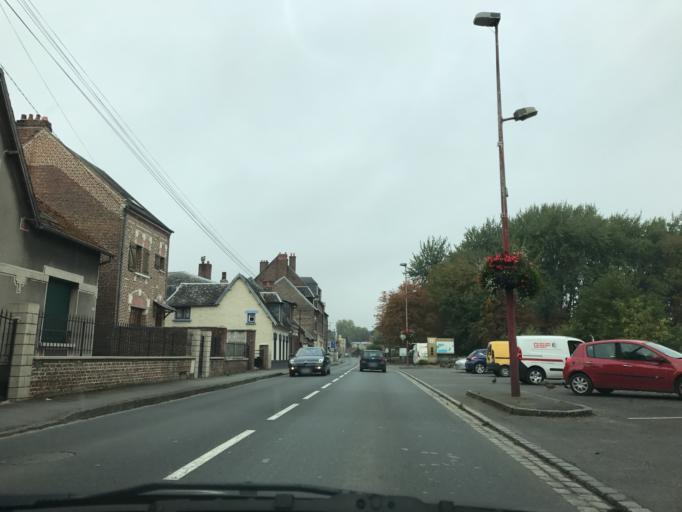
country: FR
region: Picardie
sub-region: Departement de la Somme
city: Peronne
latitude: 49.9223
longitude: 2.9324
